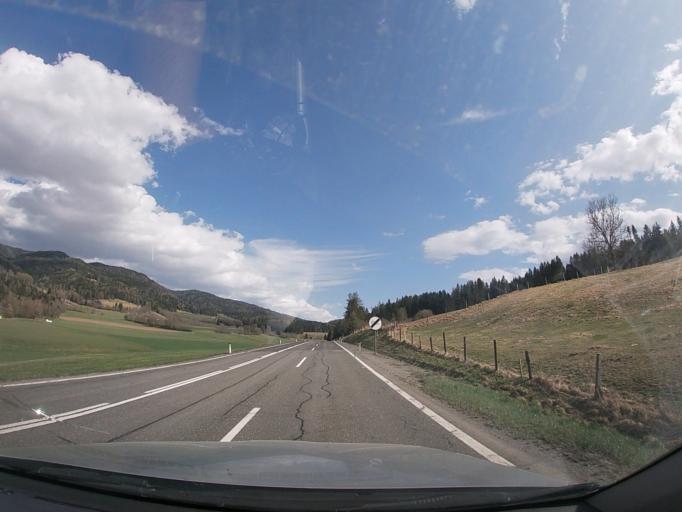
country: AT
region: Styria
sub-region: Politischer Bezirk Murau
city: Perchau am Sattel
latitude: 47.1169
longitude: 14.4524
